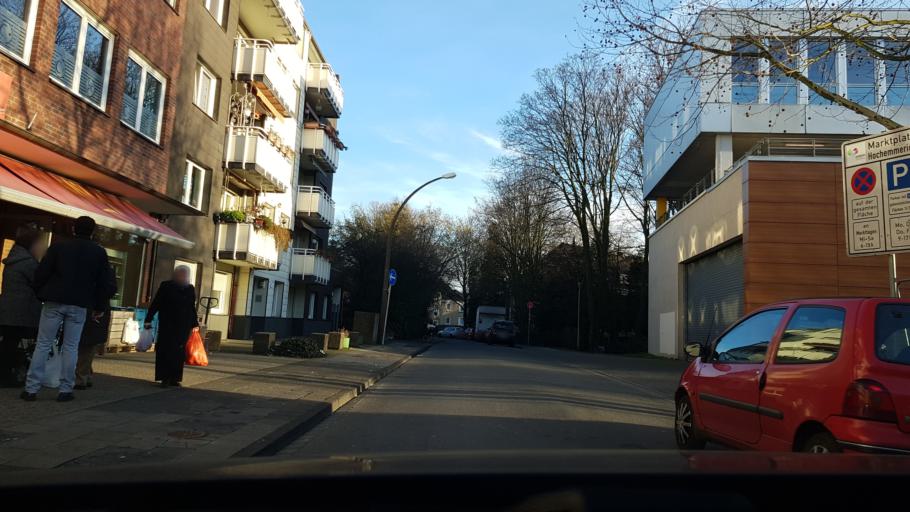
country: DE
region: North Rhine-Westphalia
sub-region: Regierungsbezirk Dusseldorf
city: Hochfeld
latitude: 51.4107
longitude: 6.7214
